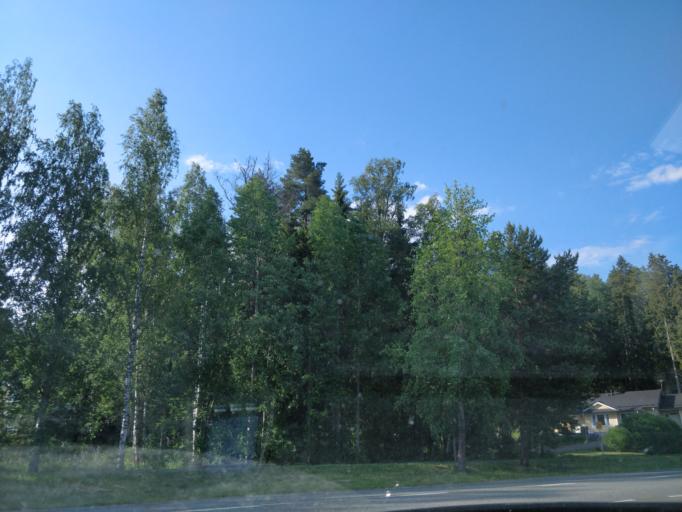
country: FI
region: Haeme
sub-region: Haemeenlinna
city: Tervakoski
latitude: 60.8067
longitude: 24.6068
